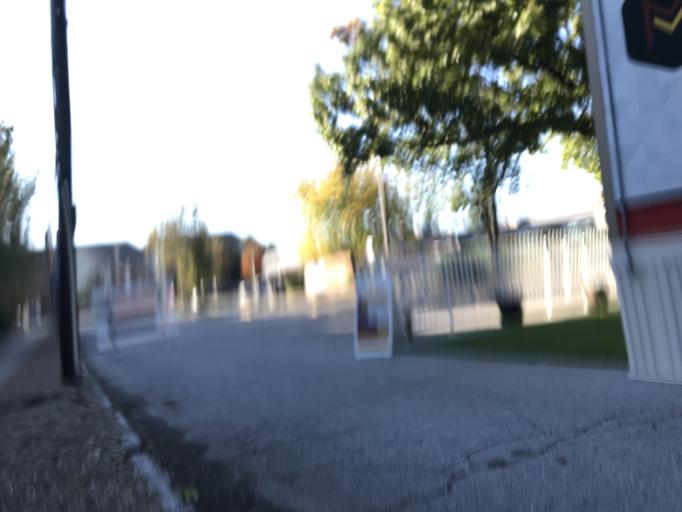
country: US
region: Kentucky
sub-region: Jefferson County
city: Louisville
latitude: 38.2193
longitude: -85.7618
